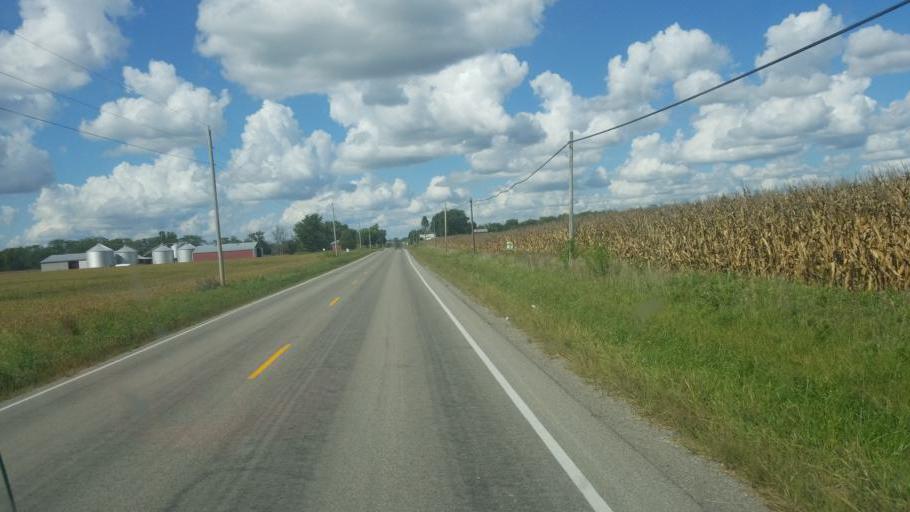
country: US
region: Ohio
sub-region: Hardin County
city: Kenton
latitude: 40.5189
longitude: -83.5739
